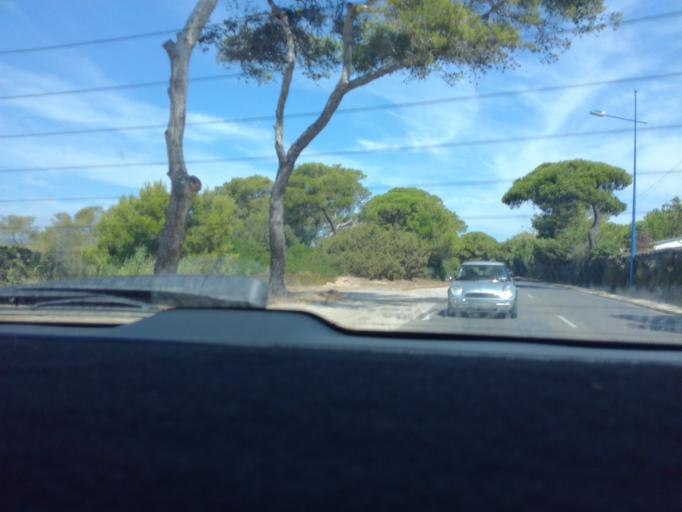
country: FR
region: Provence-Alpes-Cote d'Azur
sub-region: Departement du Var
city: Hyeres
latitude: 43.0525
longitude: 6.1469
